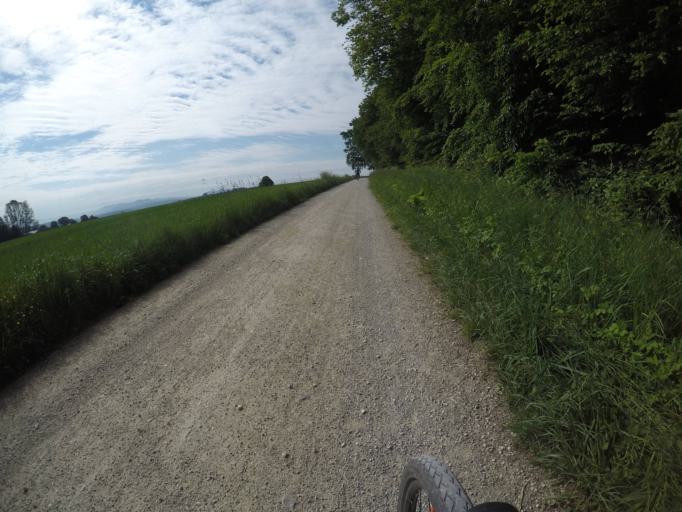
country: DE
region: Baden-Wuerttemberg
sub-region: Regierungsbezirk Stuttgart
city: Denkendorf
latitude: 48.6654
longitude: 9.3207
